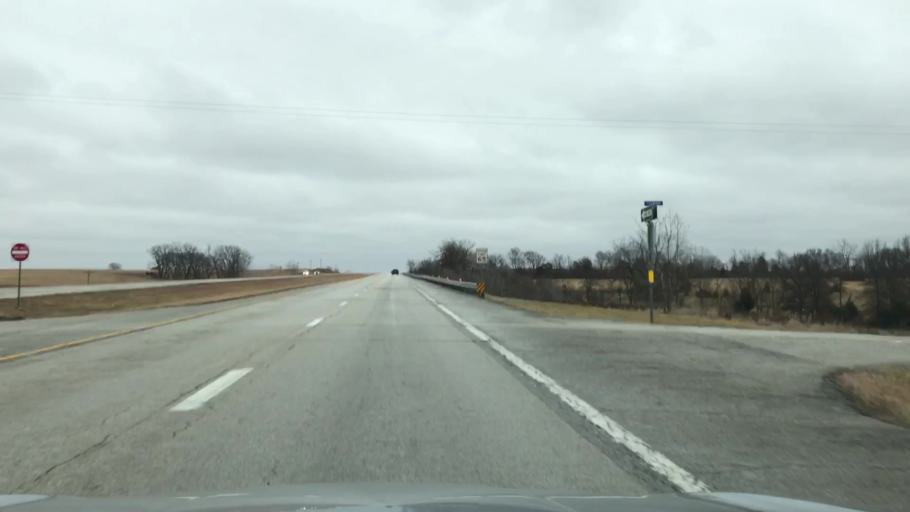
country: US
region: Missouri
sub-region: Clinton County
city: Cameron
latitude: 39.7511
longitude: -94.1485
